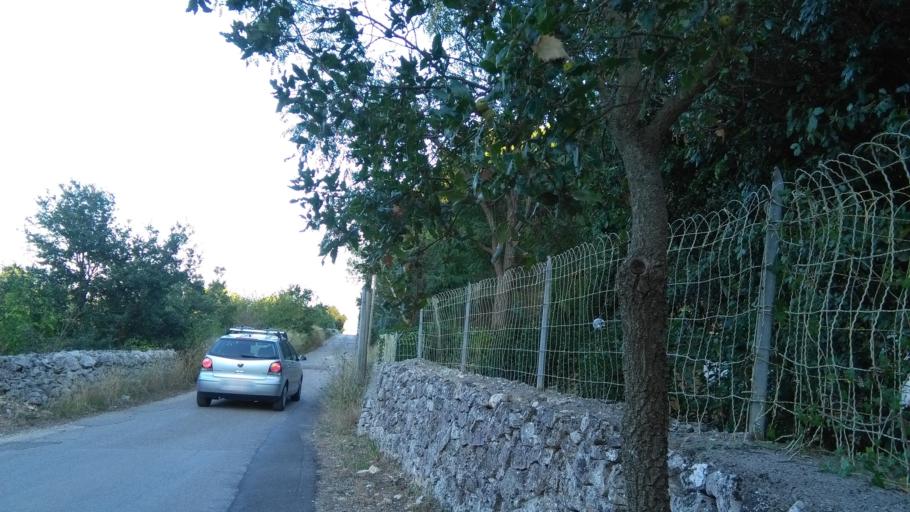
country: IT
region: Apulia
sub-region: Provincia di Bari
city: Putignano
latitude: 40.8229
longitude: 17.0903
